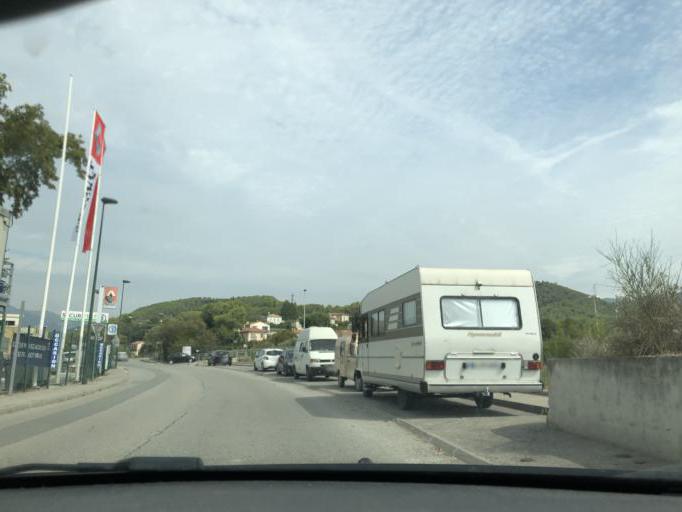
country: FR
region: Provence-Alpes-Cote d'Azur
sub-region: Departement des Alpes-Maritimes
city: Cantaron
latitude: 43.7805
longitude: 7.3371
